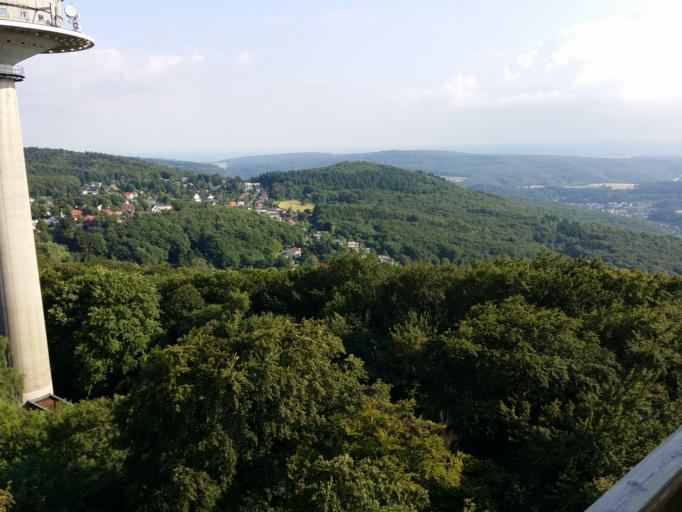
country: DE
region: Hesse
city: Eppstein
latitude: 50.1752
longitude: 8.3881
